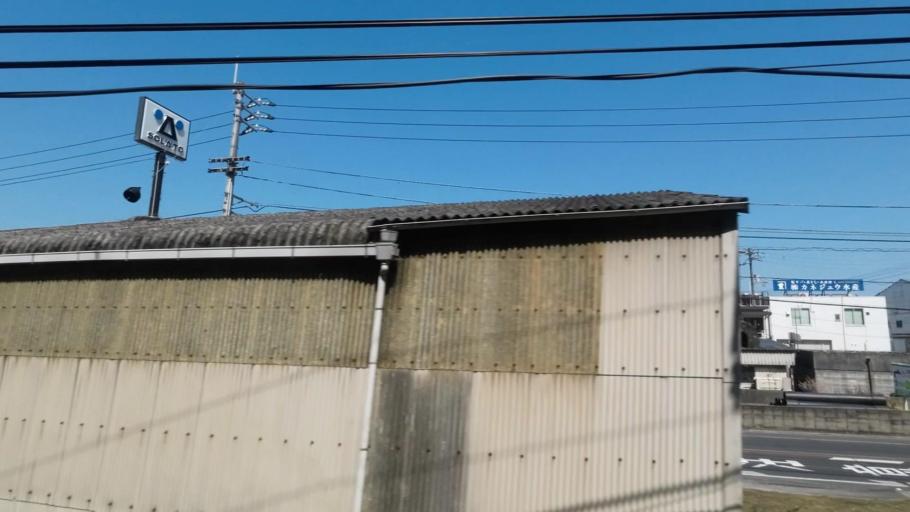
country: JP
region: Ehime
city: Kawanoecho
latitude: 34.0218
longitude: 133.5780
